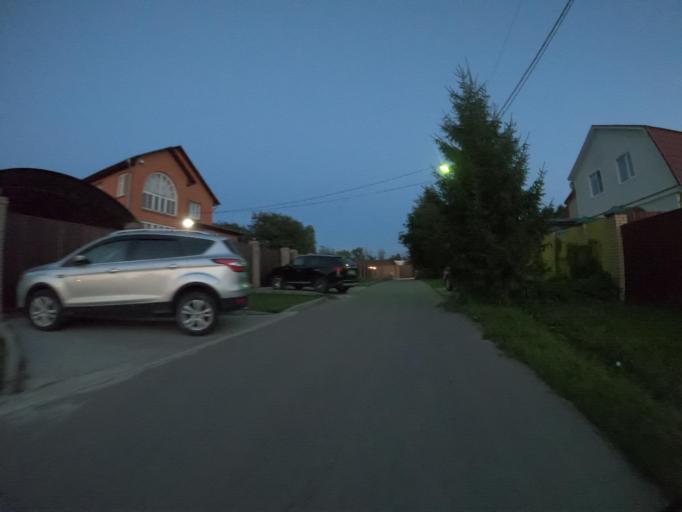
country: RU
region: Moskovskaya
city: Mikhnevo
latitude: 55.1213
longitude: 37.9500
